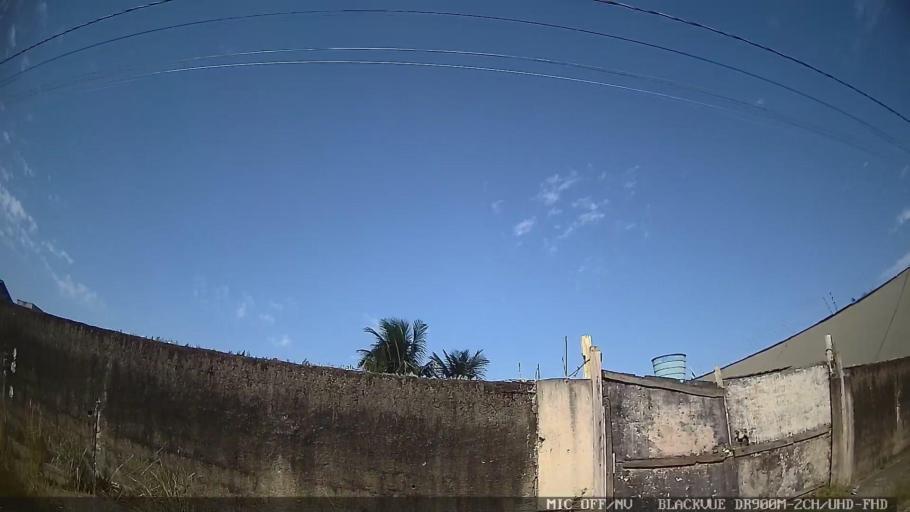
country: BR
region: Sao Paulo
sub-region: Guaruja
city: Guaruja
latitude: -23.9752
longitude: -46.2119
